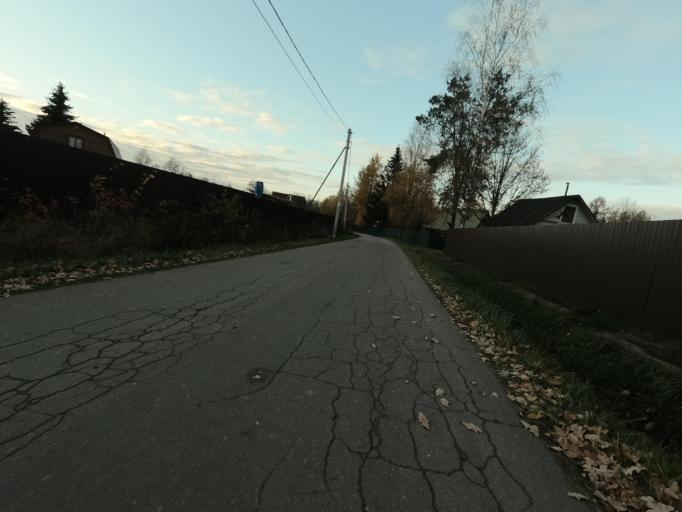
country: RU
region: Leningrad
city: Mga
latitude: 59.7799
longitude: 31.2041
